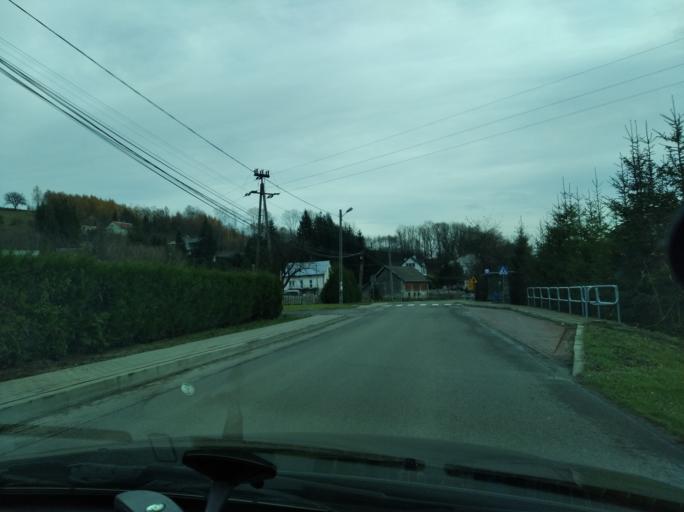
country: PL
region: Subcarpathian Voivodeship
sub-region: Powiat strzyzowski
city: Strzyzow
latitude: 49.9308
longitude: 21.7709
